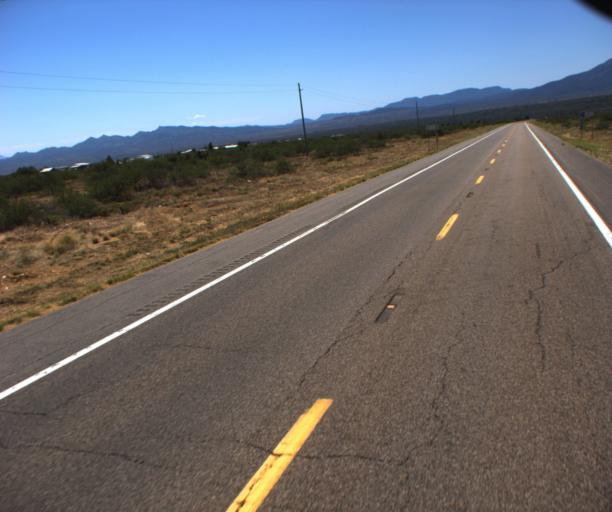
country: US
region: Arizona
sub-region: Gila County
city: Globe
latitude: 33.4367
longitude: -110.7239
